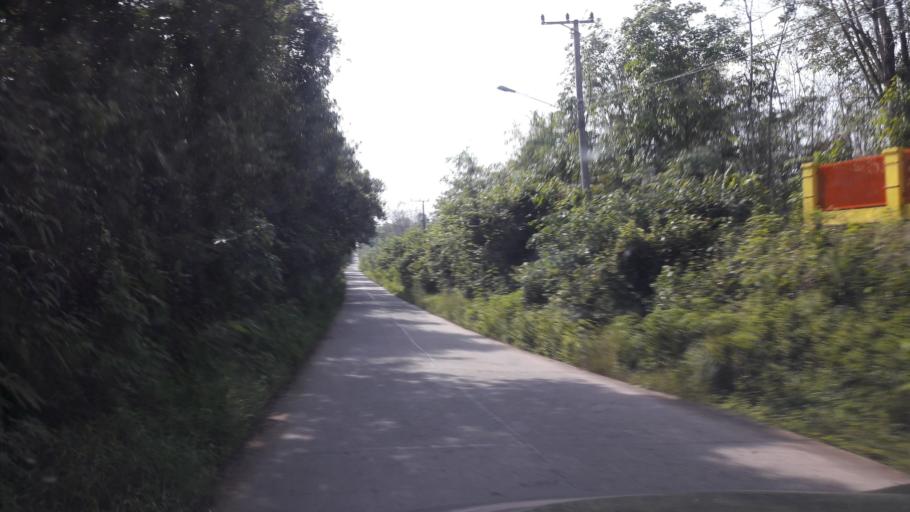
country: ID
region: South Sumatra
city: Gunungmenang
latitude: -3.3318
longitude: 104.0767
